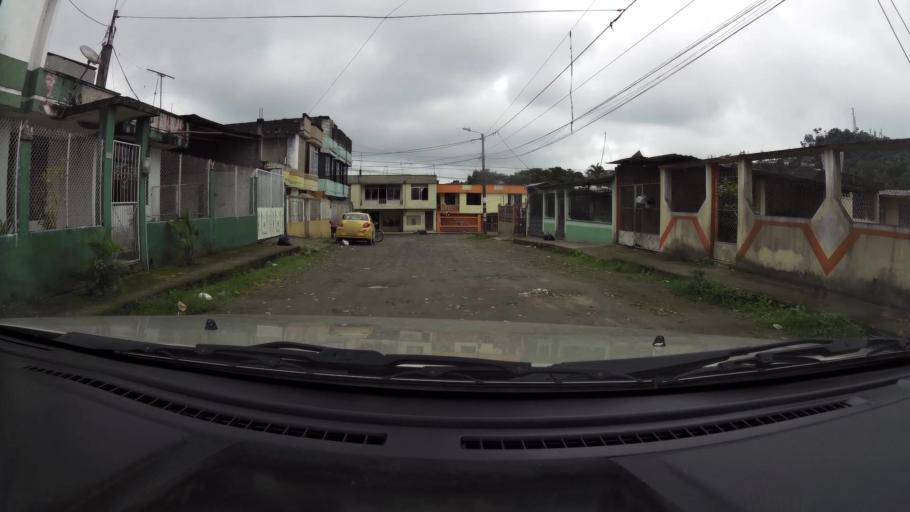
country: EC
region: Santo Domingo de los Tsachilas
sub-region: Canton Santo Domingo de los Colorados
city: Santo Domingo de los Colorados
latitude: -0.2511
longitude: -79.1979
